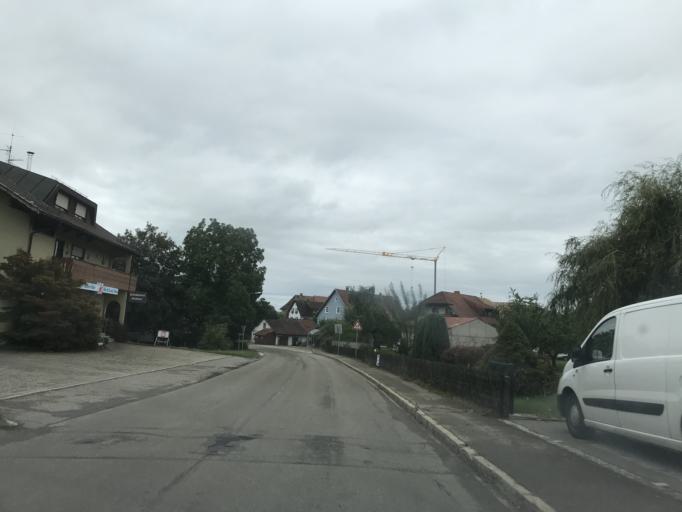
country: DE
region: Baden-Wuerttemberg
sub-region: Freiburg Region
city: Murg
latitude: 47.5836
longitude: 8.0320
